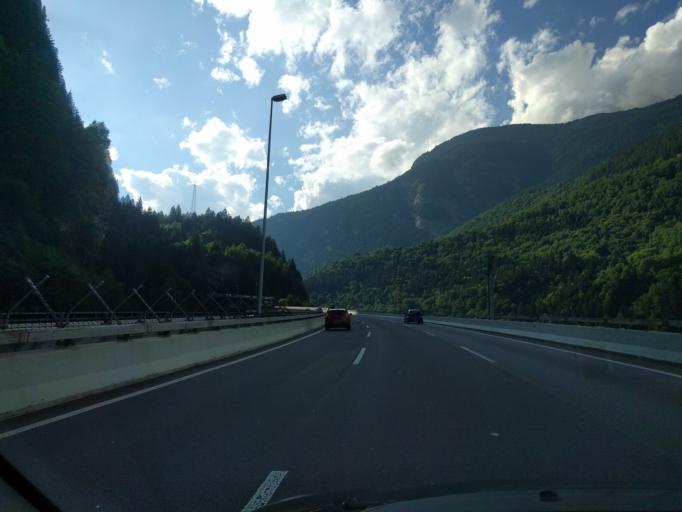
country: CH
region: Ticino
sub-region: Leventina District
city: Faido
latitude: 46.4861
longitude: 8.7764
